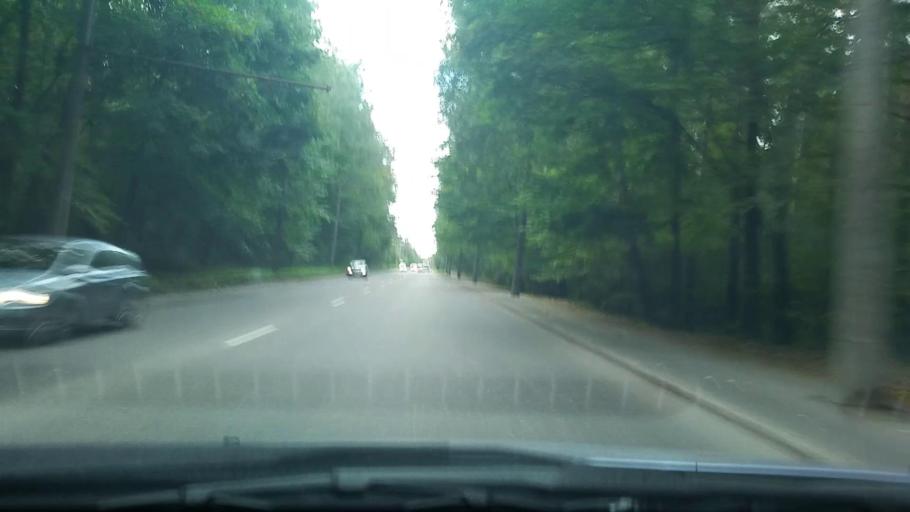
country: LV
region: Riga
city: Jaunciems
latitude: 56.9660
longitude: 24.2052
